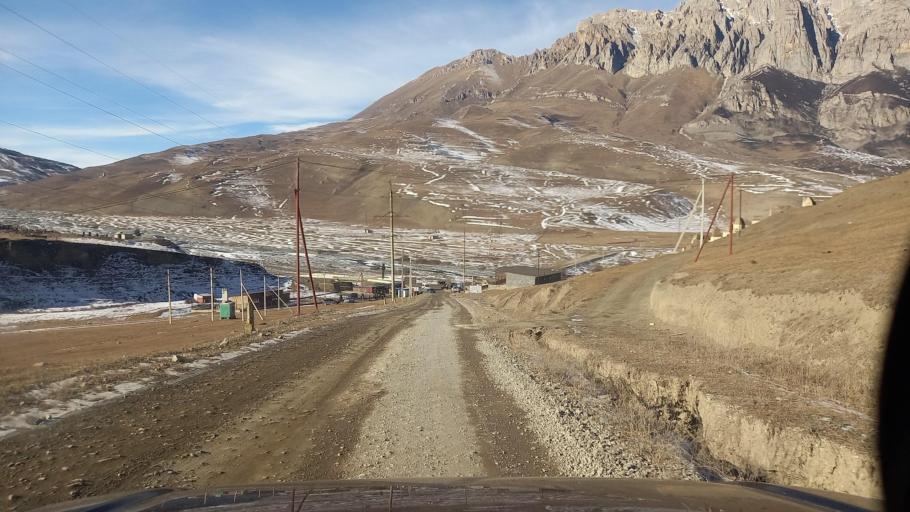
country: RU
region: North Ossetia
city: Verkhniy Fiagdon
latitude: 42.8395
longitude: 44.4479
